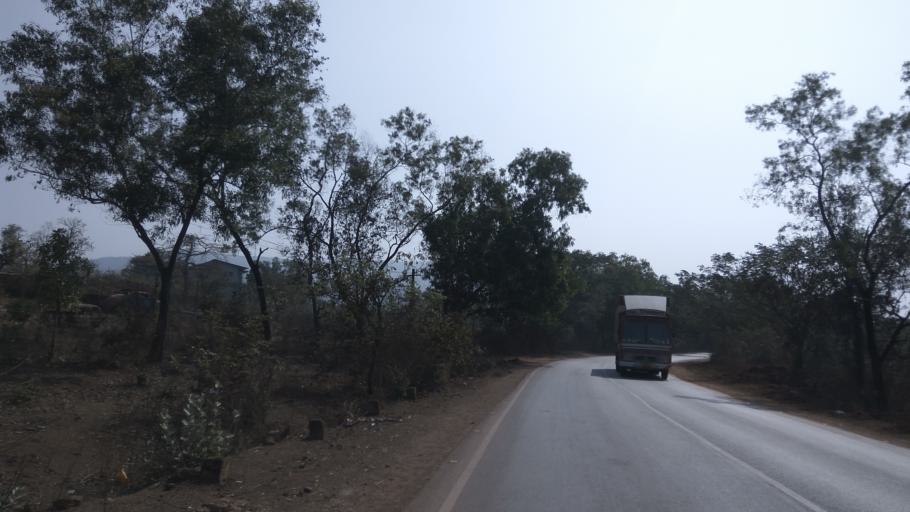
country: IN
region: Goa
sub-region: North Goa
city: Palle
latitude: 15.4148
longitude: 74.0780
